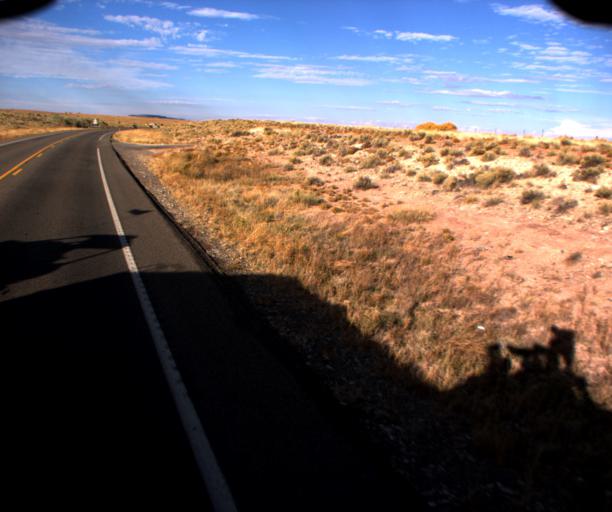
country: US
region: New Mexico
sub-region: San Juan County
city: Shiprock
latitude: 36.9266
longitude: -109.1717
